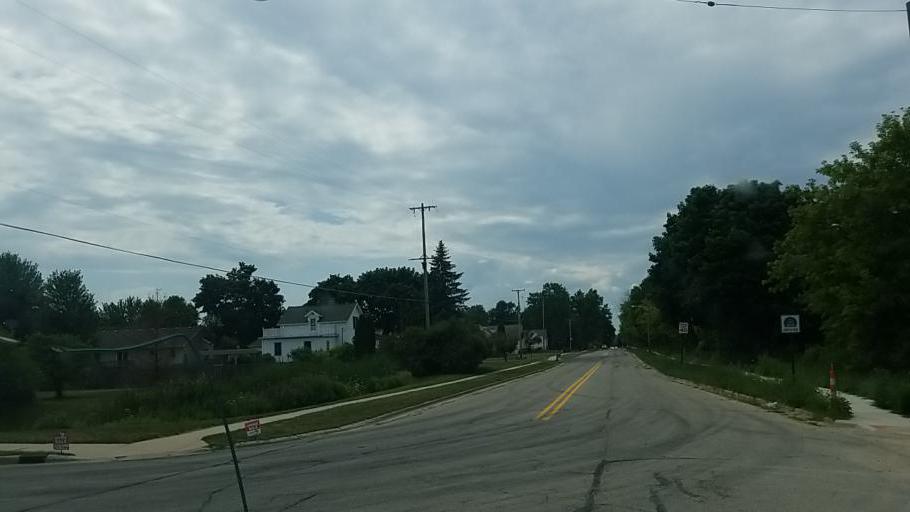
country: US
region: Michigan
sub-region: Kent County
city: Walker
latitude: 43.0012
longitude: -85.7524
